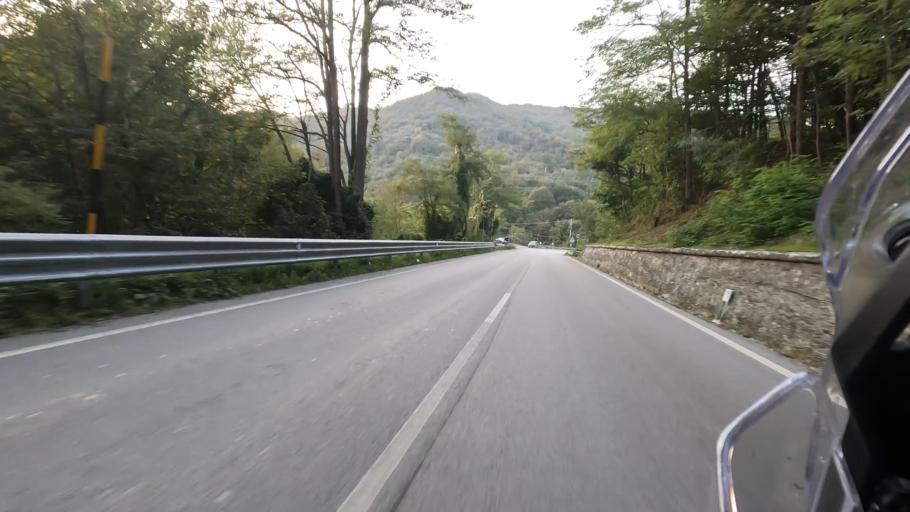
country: IT
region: Liguria
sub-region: Provincia di Savona
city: Osteria dei Cacciatori-Stella
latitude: 44.4474
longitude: 8.4782
